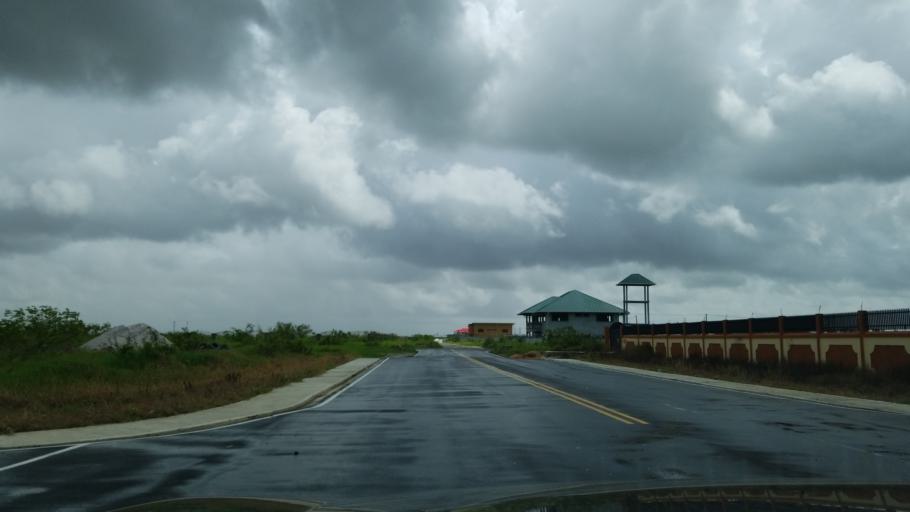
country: GY
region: Demerara-Mahaica
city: Georgetown
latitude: 6.7508
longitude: -58.1631
